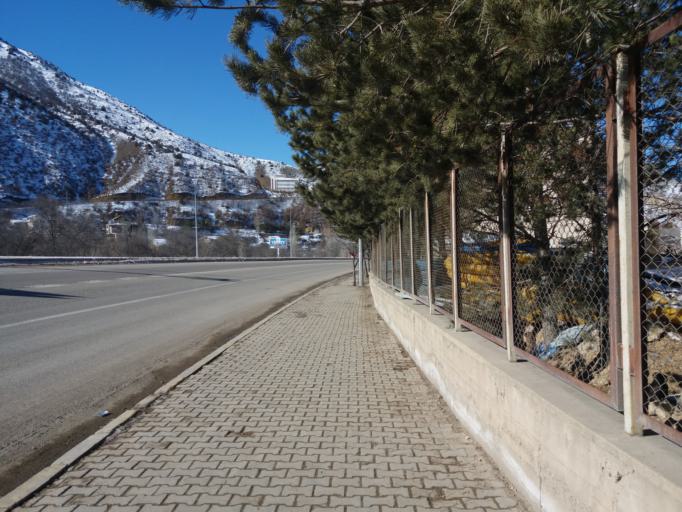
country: TR
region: Gumushane
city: Gumushkhane
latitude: 40.4368
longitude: 39.5078
